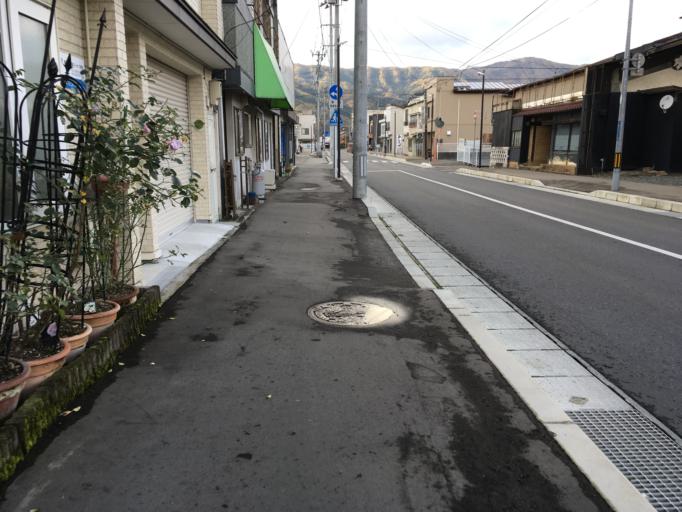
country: JP
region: Iwate
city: Tono
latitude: 39.3308
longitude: 141.5334
